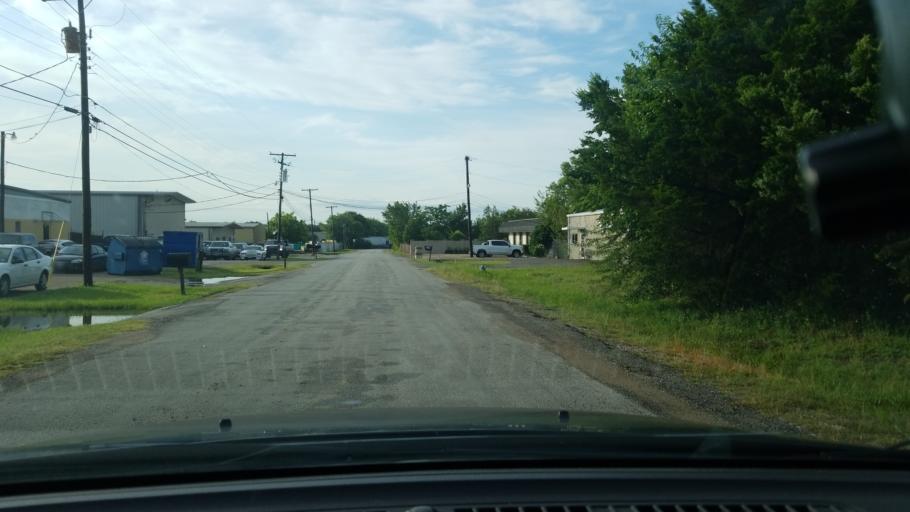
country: US
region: Texas
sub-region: Dallas County
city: Mesquite
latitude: 32.7961
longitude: -96.6211
